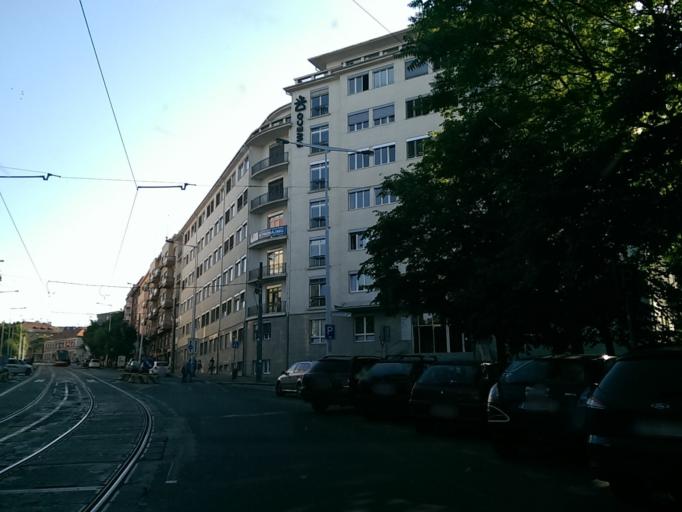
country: CZ
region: Praha
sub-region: Praha 2
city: Vysehrad
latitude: 50.0626
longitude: 14.4381
